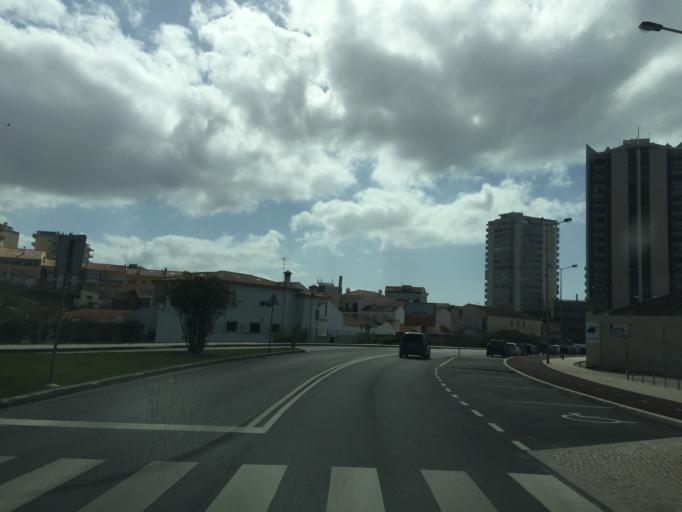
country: PT
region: Coimbra
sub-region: Figueira da Foz
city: Buarcos
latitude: 40.1653
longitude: -8.8716
